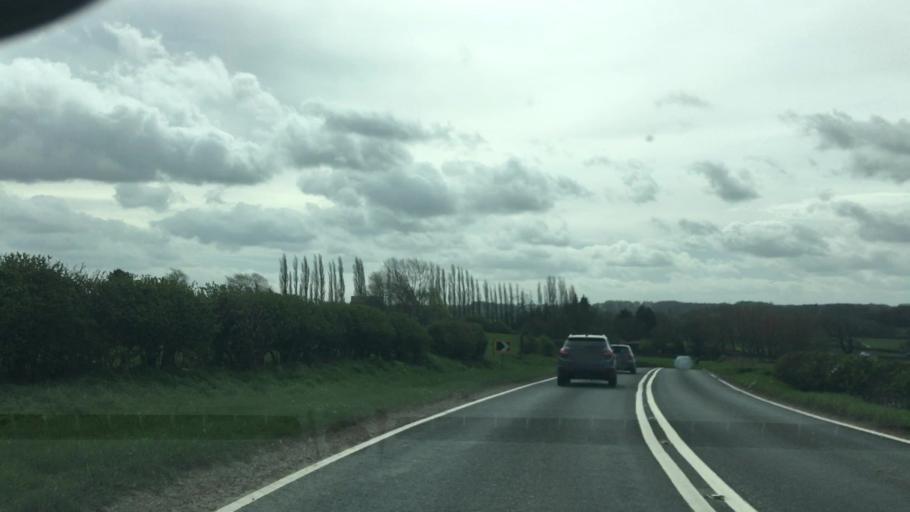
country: GB
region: England
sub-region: North Yorkshire
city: Knaresborough
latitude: 53.9597
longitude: -1.4427
